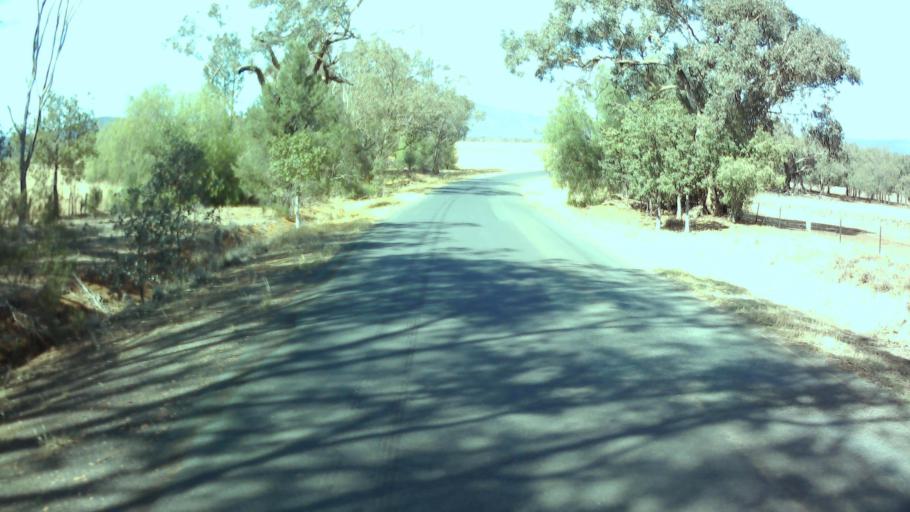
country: AU
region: New South Wales
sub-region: Weddin
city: Grenfell
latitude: -33.9308
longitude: 148.0946
